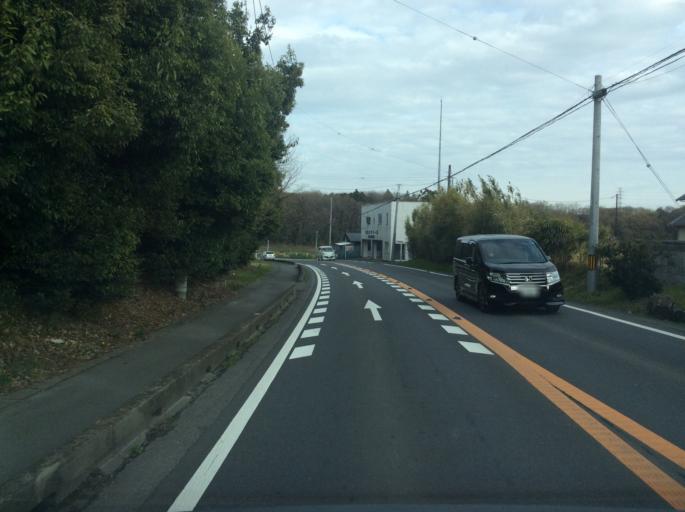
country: JP
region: Ibaraki
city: Tsukuba
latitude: 36.1802
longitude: 140.0443
